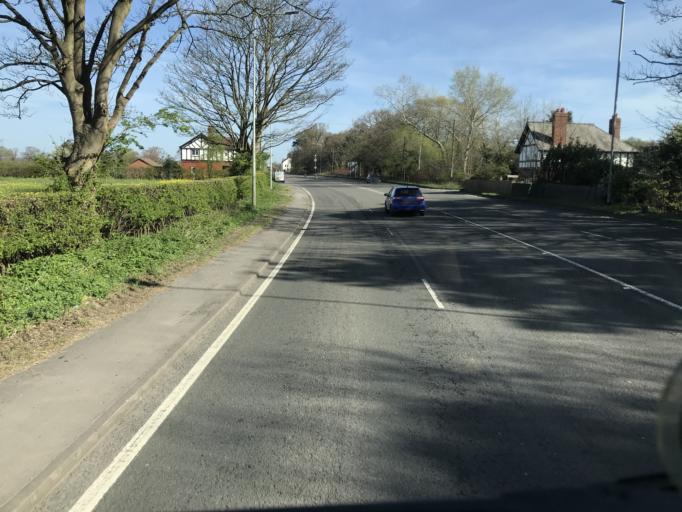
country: GB
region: England
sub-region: Cheshire East
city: Mere
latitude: 53.2989
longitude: -2.4198
